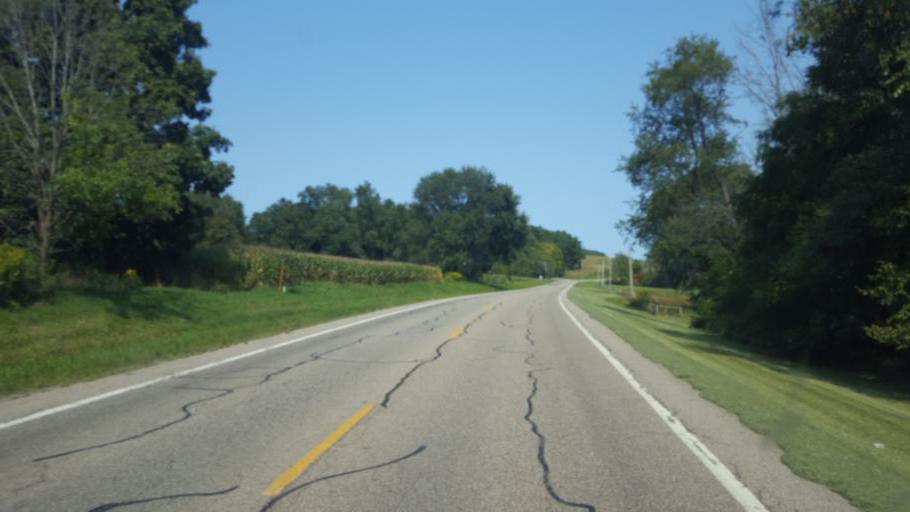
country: US
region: Ohio
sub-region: Knox County
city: Danville
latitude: 40.4918
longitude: -82.3513
